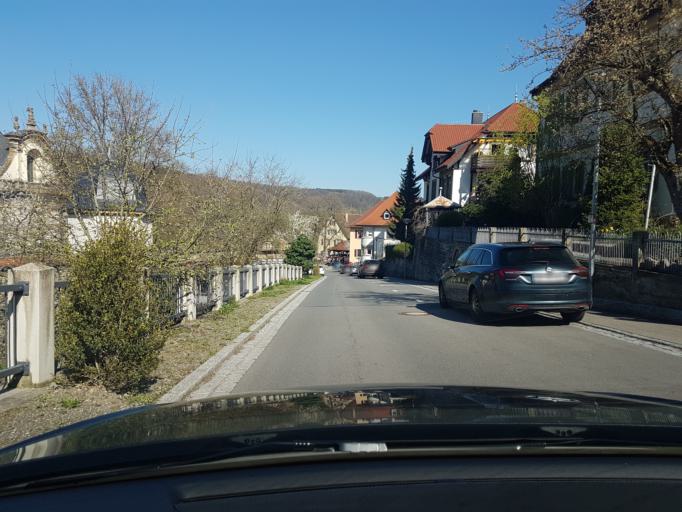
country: DE
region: Baden-Wuerttemberg
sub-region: Regierungsbezirk Stuttgart
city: Jagsthausen
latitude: 49.3287
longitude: 9.5071
